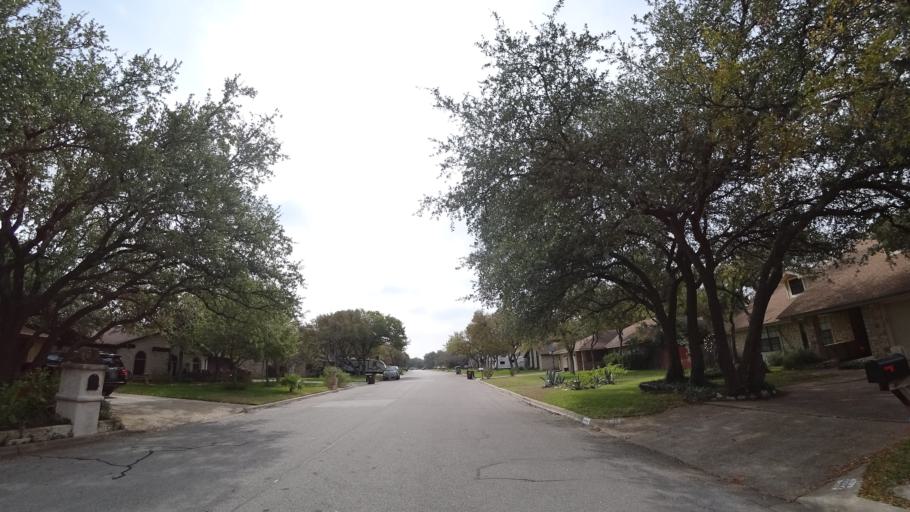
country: US
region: Texas
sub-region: Williamson County
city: Round Rock
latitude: 30.4977
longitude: -97.6937
